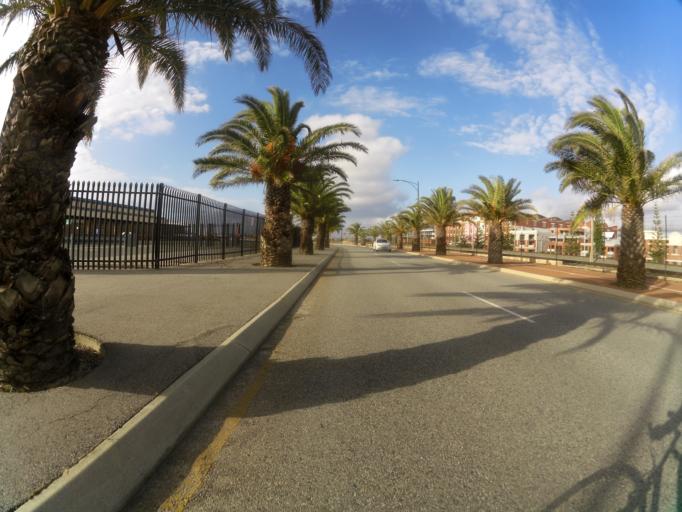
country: AU
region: Western Australia
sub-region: Fremantle
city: North Fremantle
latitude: -32.0482
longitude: 115.7485
